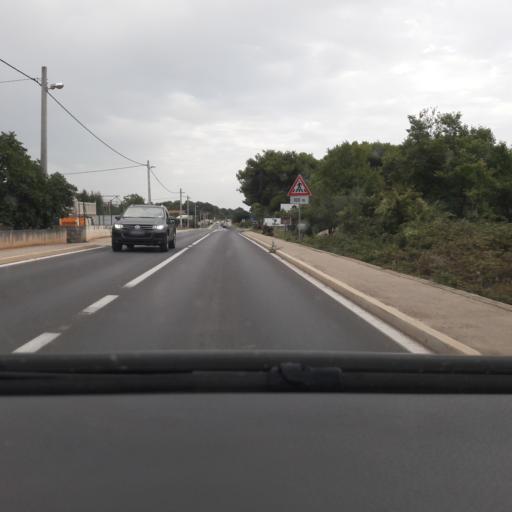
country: HR
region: Zadarska
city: Nin
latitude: 44.1698
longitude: 15.1960
